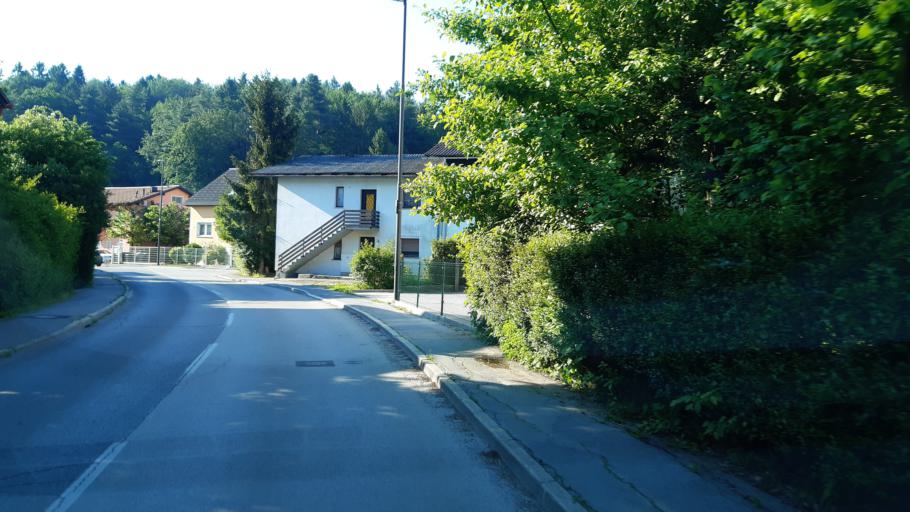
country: SI
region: Trzin
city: Trzin
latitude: 46.1058
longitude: 14.5259
